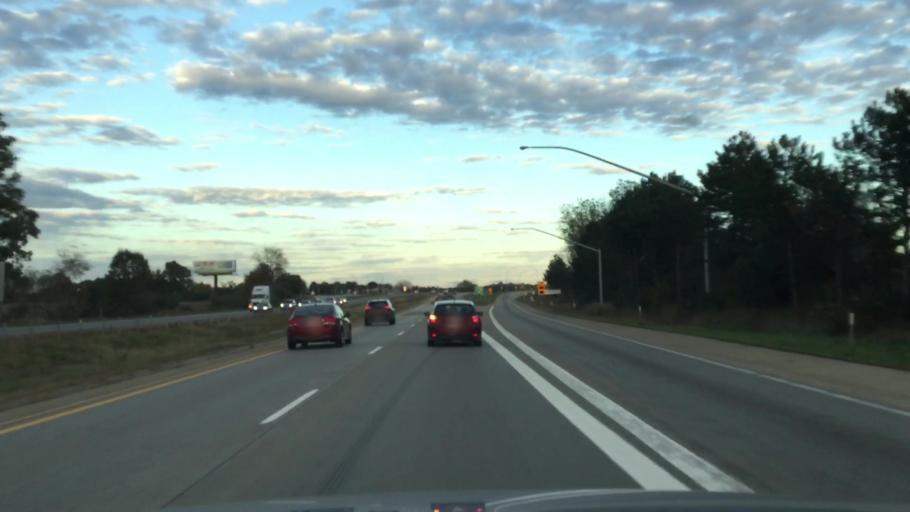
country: US
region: Michigan
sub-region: Jackson County
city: Grass Lake
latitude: 42.2918
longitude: -84.1856
